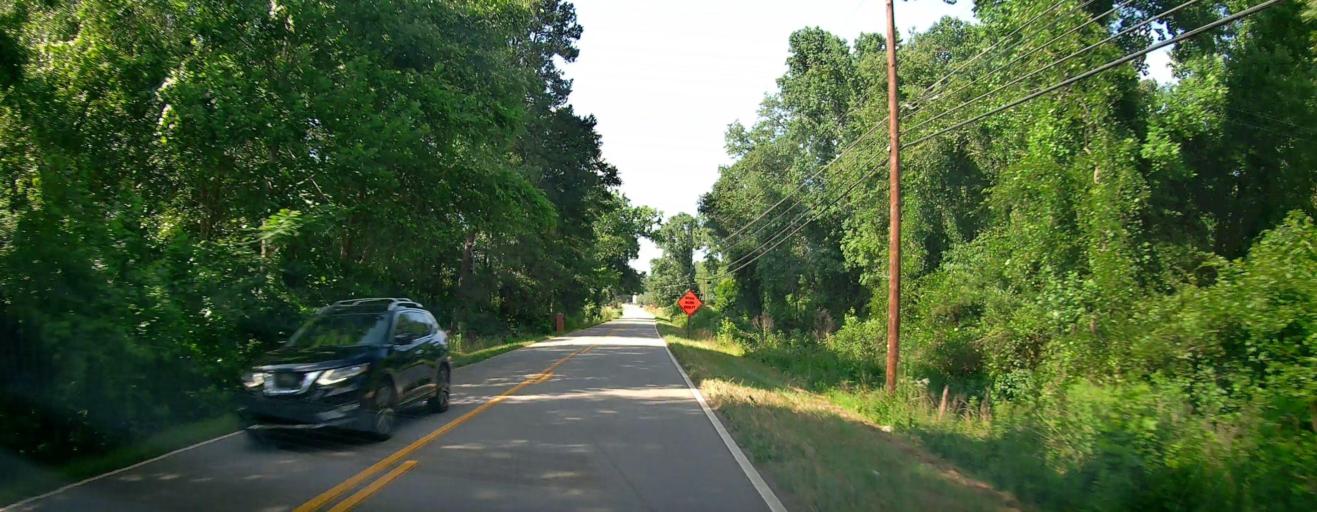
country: US
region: Georgia
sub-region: Henry County
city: McDonough
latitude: 33.4557
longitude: -84.2309
